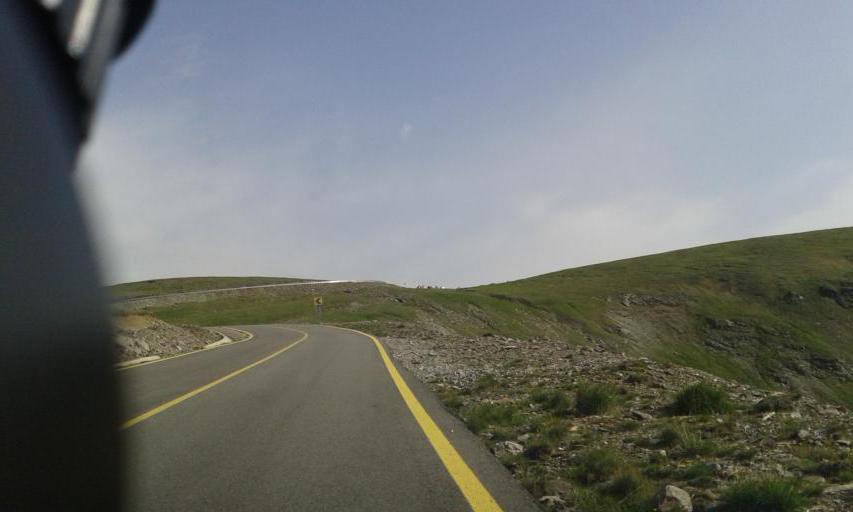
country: RO
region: Gorj
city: Novaci-Straini
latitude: 45.3763
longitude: 23.6534
